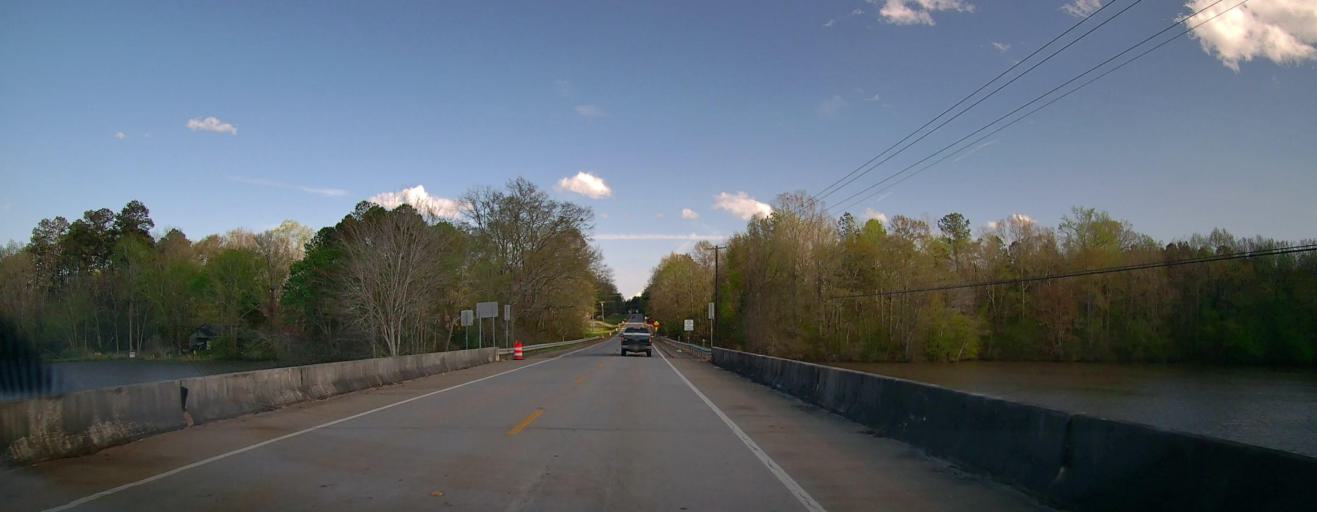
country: US
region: Georgia
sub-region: Putnam County
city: Eatonton
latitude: 33.1817
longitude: -83.4105
